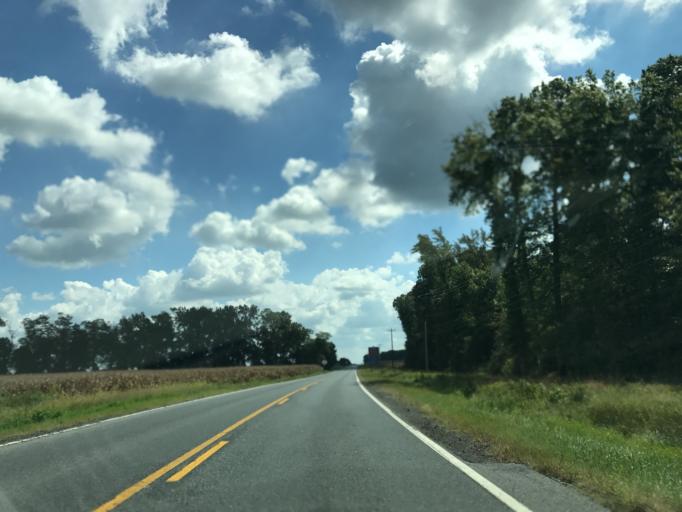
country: US
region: Maryland
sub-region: Queen Anne's County
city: Centreville
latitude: 39.0256
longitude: -76.0188
